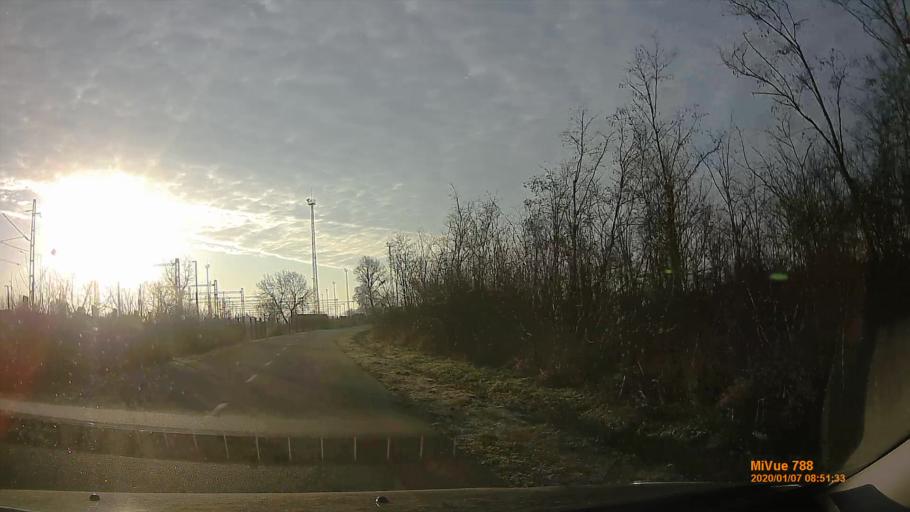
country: HU
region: Gyor-Moson-Sopron
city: Rajka
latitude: 48.0004
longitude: 17.1880
